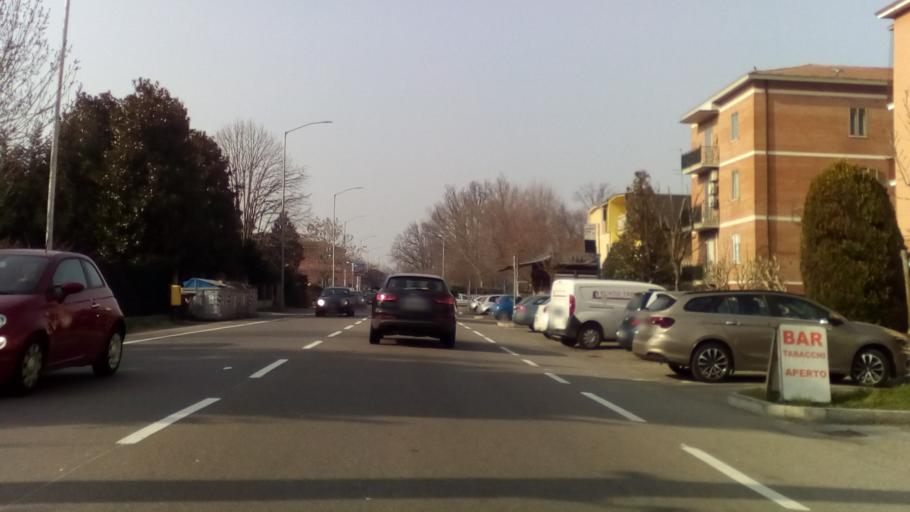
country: IT
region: Emilia-Romagna
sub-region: Provincia di Modena
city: Modena
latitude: 44.6263
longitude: 10.9489
